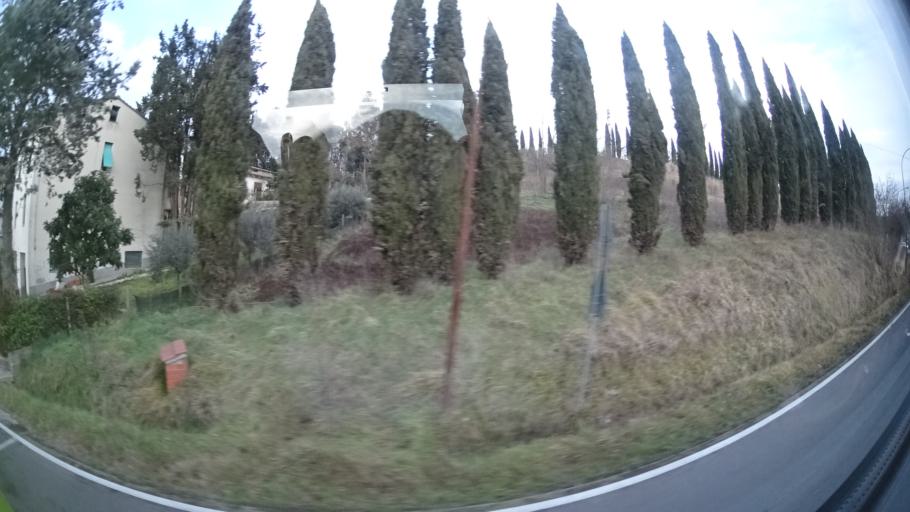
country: IT
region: Tuscany
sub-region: Provincia di Siena
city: Poggibonsi
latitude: 43.4689
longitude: 11.1569
